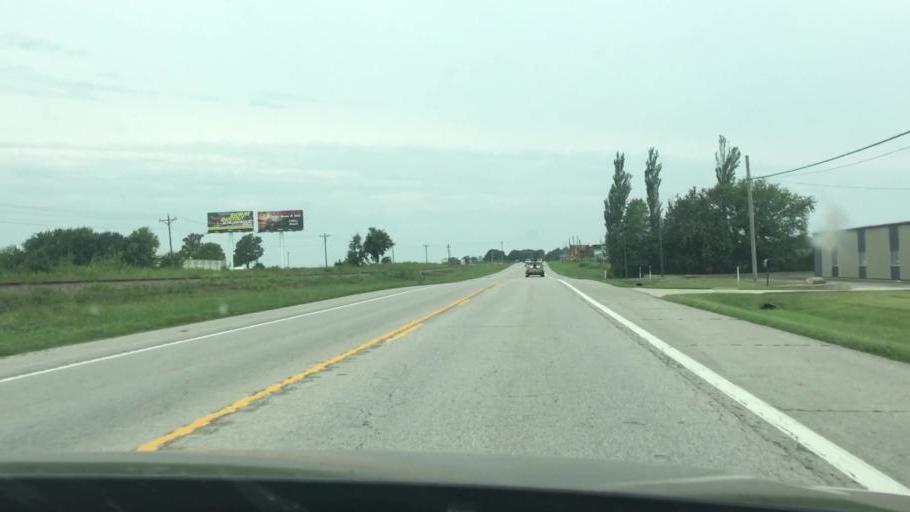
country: US
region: Missouri
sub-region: Pettis County
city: Sedalia
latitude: 38.6960
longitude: -93.1671
